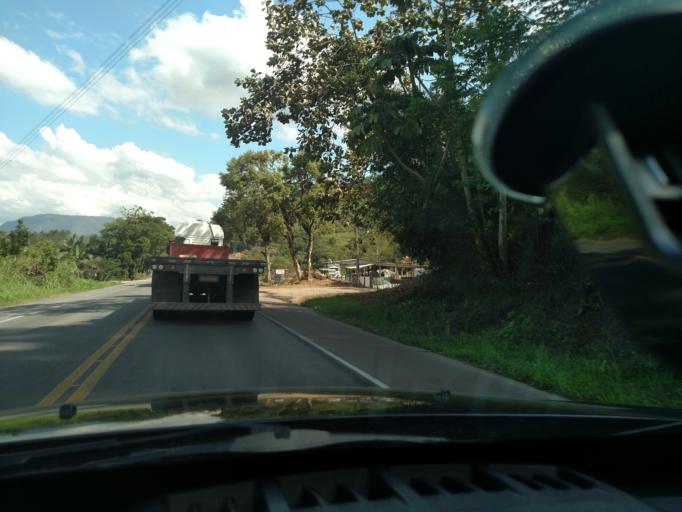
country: BR
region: Santa Catarina
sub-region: Rodeio
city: Gavea
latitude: -26.9534
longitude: -49.3265
